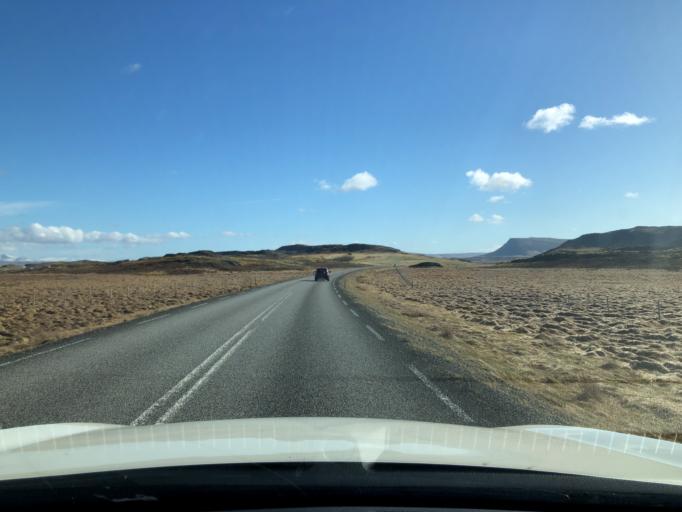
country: IS
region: West
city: Borgarnes
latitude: 64.5687
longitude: -21.6846
